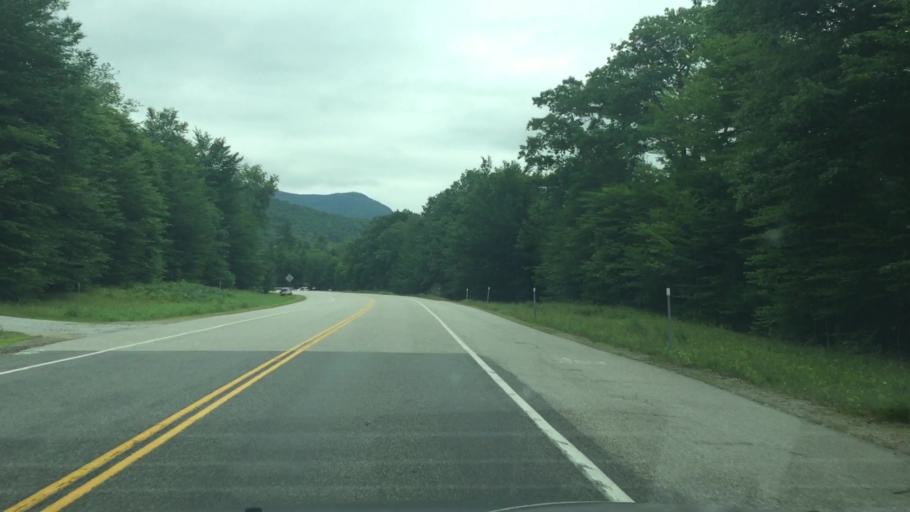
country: US
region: New Hampshire
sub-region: Carroll County
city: North Conway
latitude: 44.0826
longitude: -71.3473
